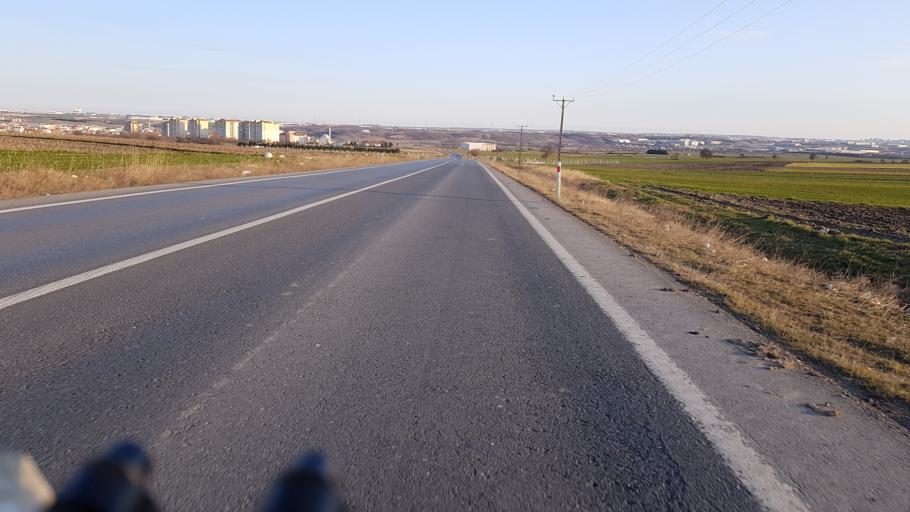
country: TR
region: Tekirdag
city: Velimese
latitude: 41.2600
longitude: 27.8588
